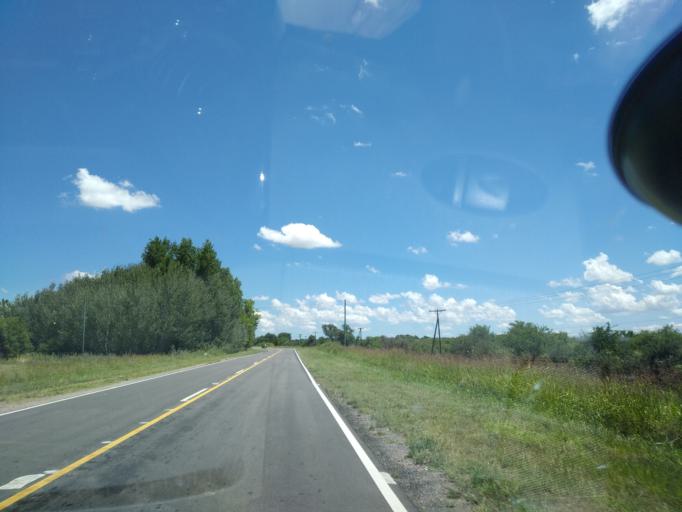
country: AR
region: Cordoba
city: Salsacate
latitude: -31.3626
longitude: -65.1051
